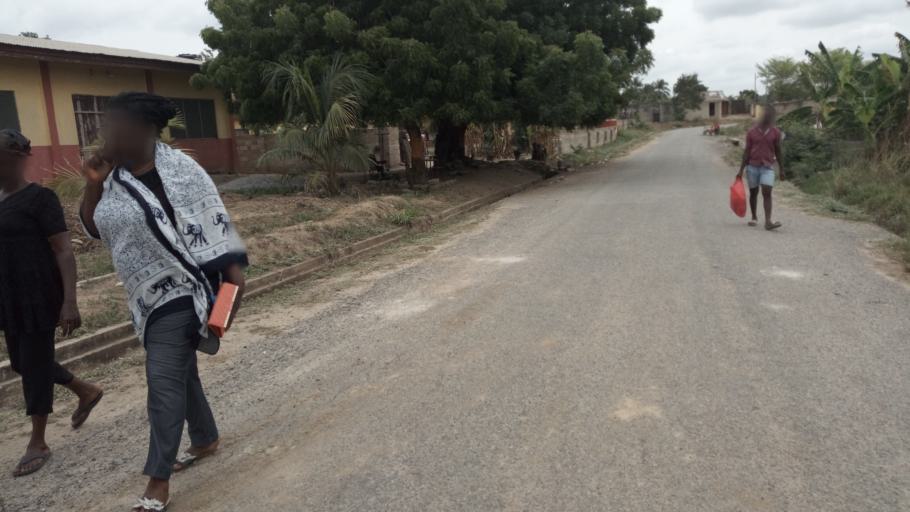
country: GH
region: Central
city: Winneba
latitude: 5.3806
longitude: -0.6402
